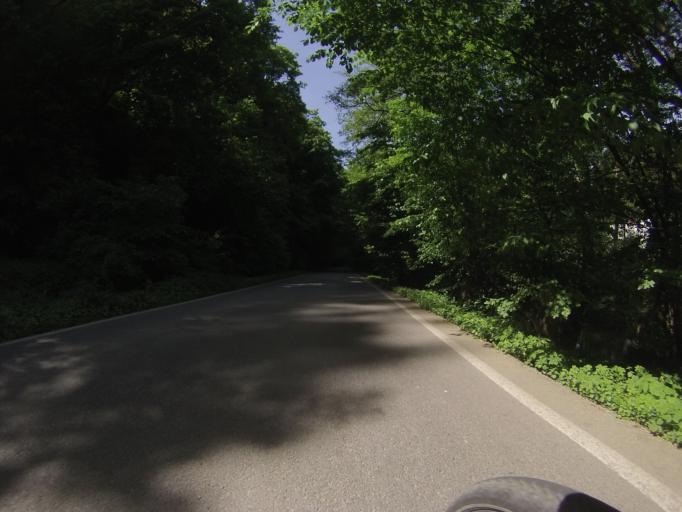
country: CZ
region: South Moravian
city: Bilovice nad Svitavou
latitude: 49.2726
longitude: 16.6643
